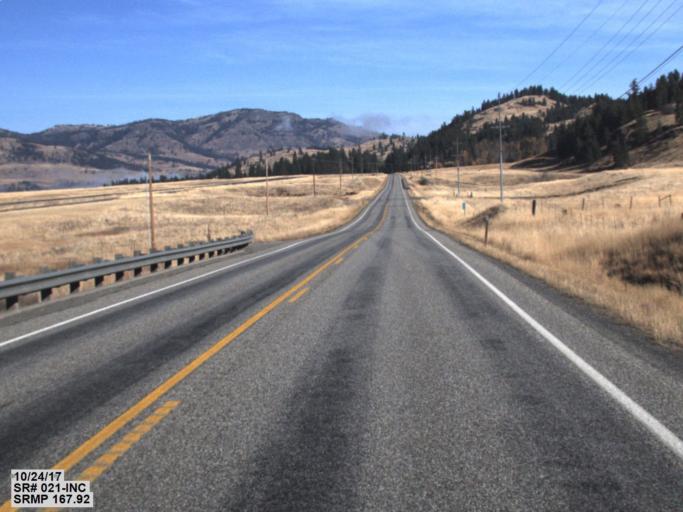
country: US
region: Washington
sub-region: Ferry County
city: Republic
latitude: 48.7146
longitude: -118.6552
